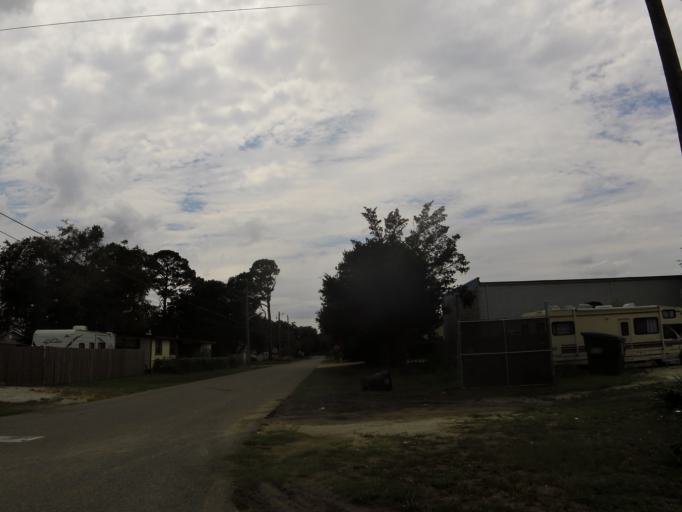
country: US
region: Florida
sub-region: Duval County
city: Atlantic Beach
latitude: 30.3350
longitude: -81.4202
